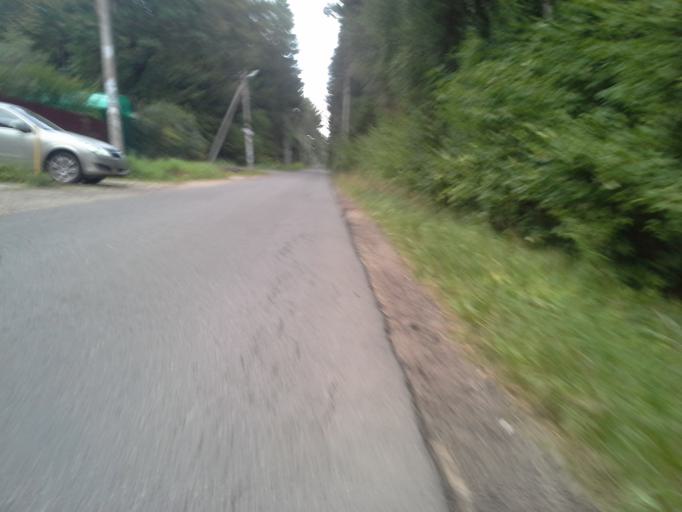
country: RU
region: Moskovskaya
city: Zhavoronki
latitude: 55.6334
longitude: 37.0724
